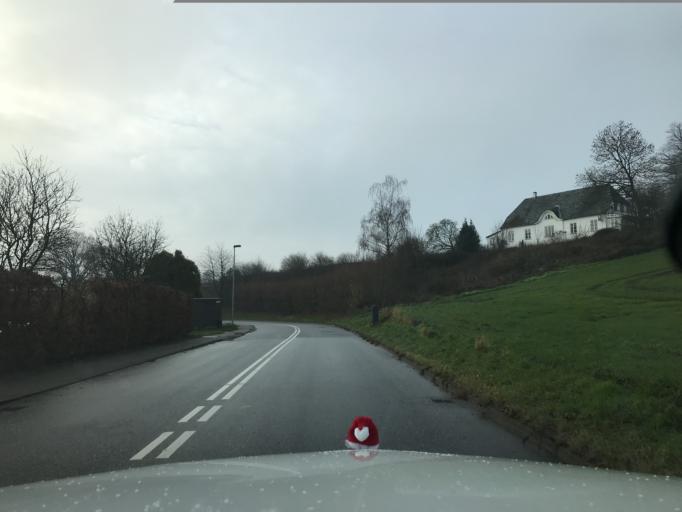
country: DK
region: South Denmark
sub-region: Sonderborg Kommune
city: Grasten
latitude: 54.8991
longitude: 9.5675
